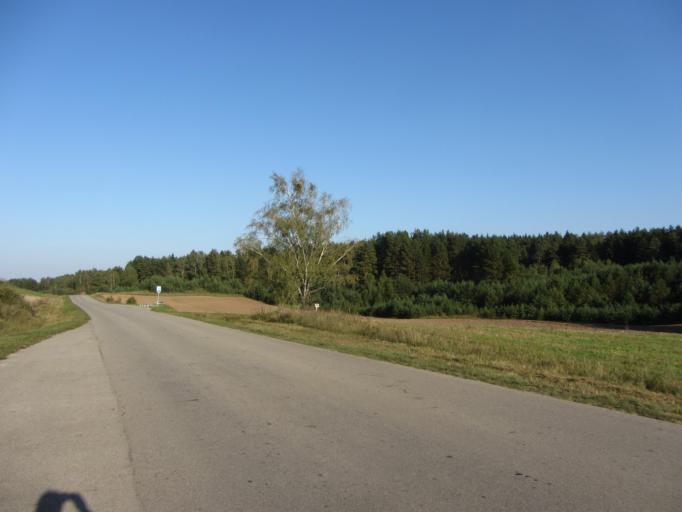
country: LT
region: Alytaus apskritis
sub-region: Alytaus rajonas
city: Daugai
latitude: 54.2378
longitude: 24.3117
